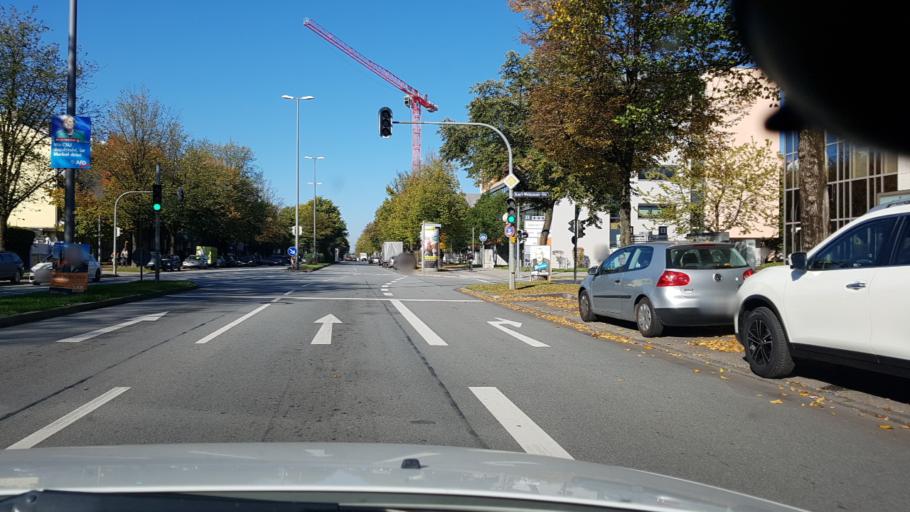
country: DE
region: Bavaria
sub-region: Upper Bavaria
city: Bogenhausen
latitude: 48.1798
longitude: 11.5851
